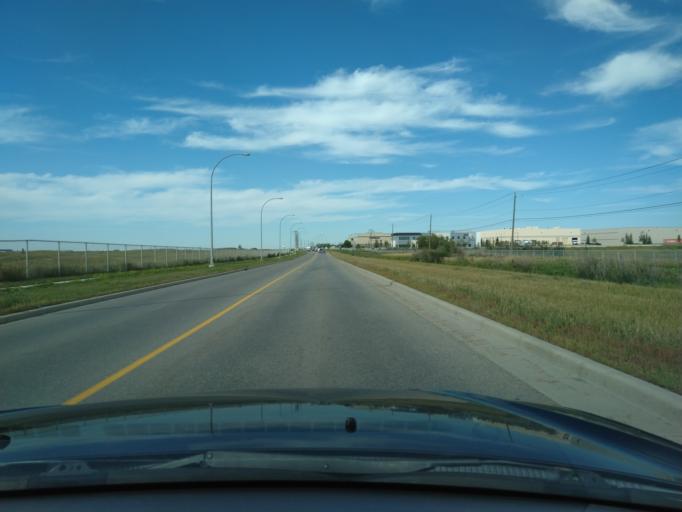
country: CA
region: Alberta
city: Calgary
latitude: 51.1054
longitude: -113.9823
